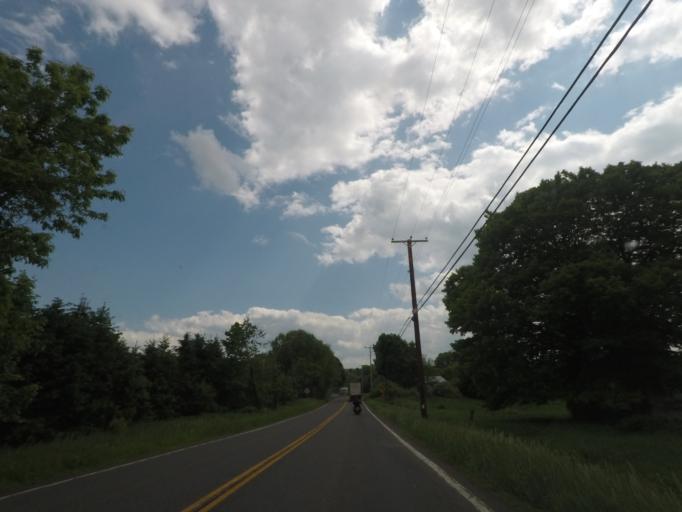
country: US
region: New York
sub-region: Dutchess County
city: Pine Plains
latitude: 42.0426
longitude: -73.6169
